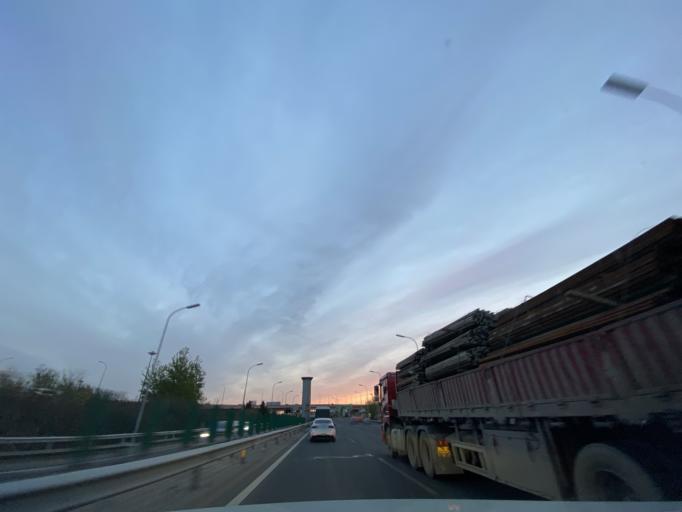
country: CN
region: Beijing
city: Qinghe
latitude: 40.0210
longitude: 116.3263
